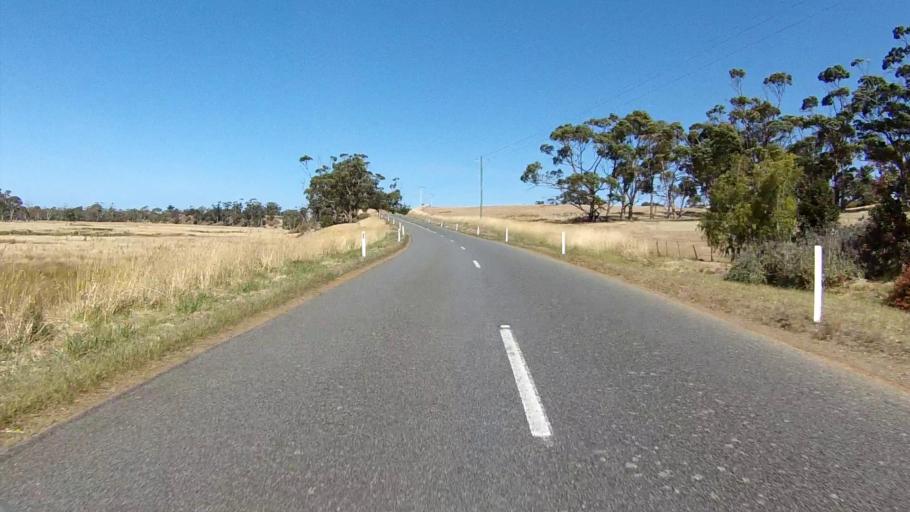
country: AU
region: Tasmania
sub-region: Sorell
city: Sorell
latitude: -42.2650
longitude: 148.0025
